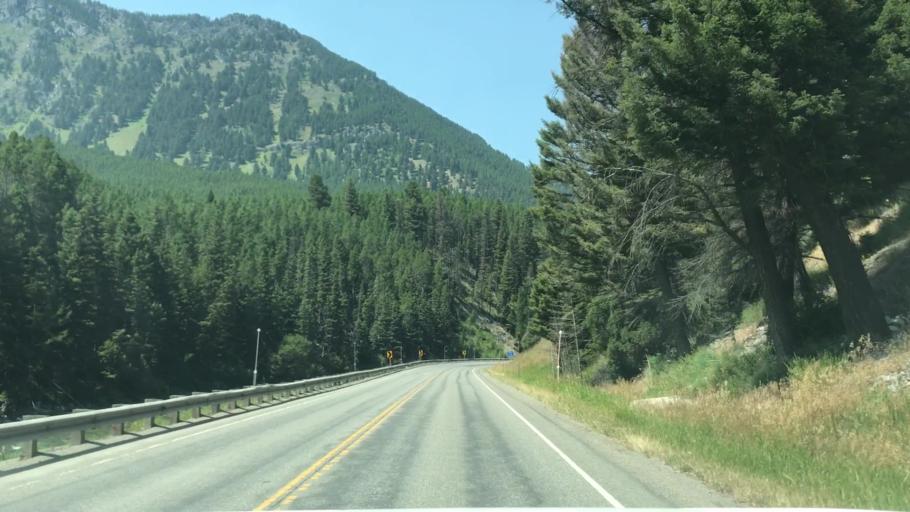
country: US
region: Montana
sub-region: Gallatin County
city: Big Sky
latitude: 45.3817
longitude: -111.1907
